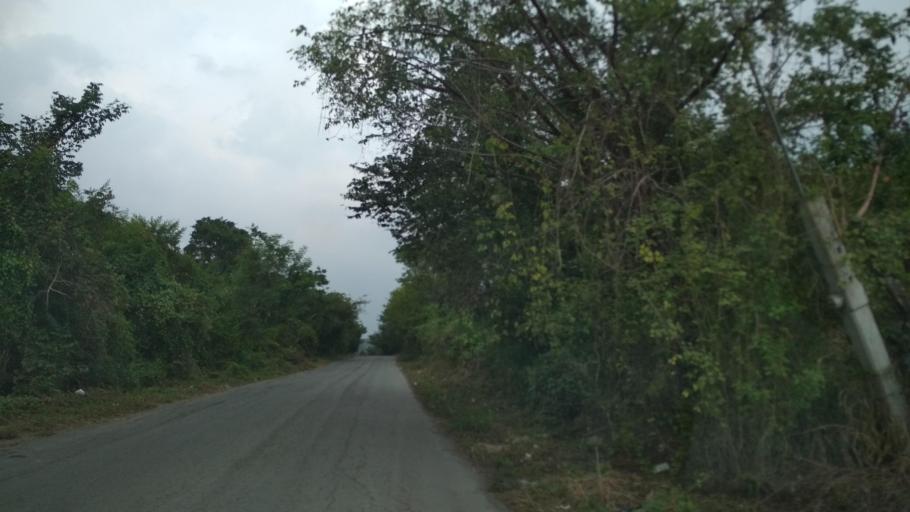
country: MM
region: Kayah
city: Loikaw
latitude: 20.2416
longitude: 97.2745
